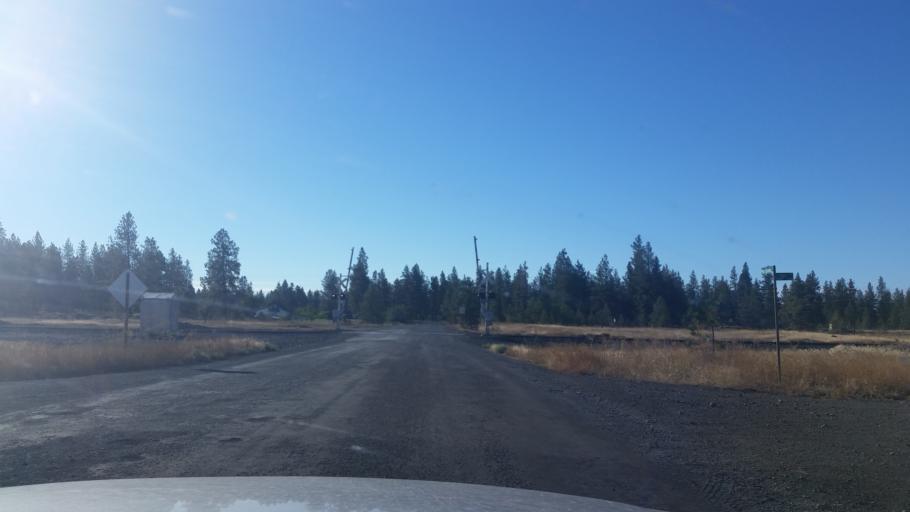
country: US
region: Washington
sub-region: Spokane County
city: Medical Lake
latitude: 47.4347
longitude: -117.7824
